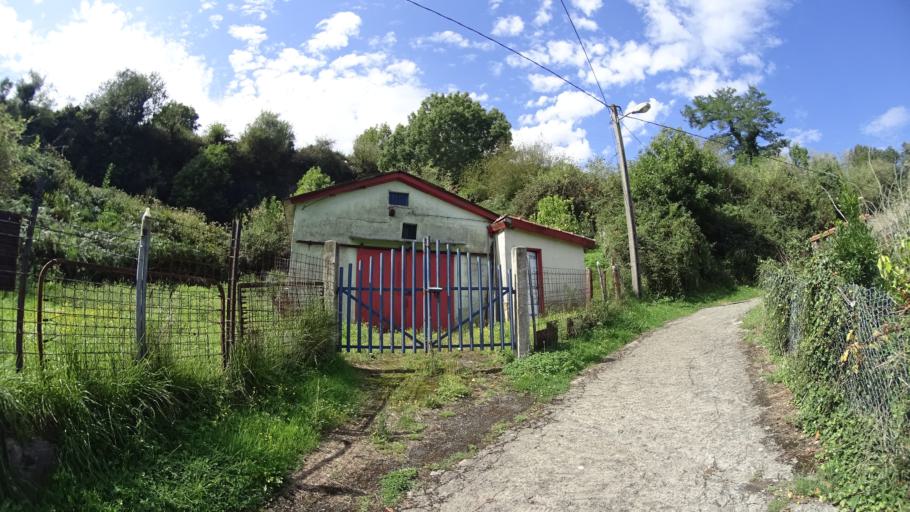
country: ES
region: Basque Country
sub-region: Bizkaia
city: Urtuella
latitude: 43.2834
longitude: -3.0573
